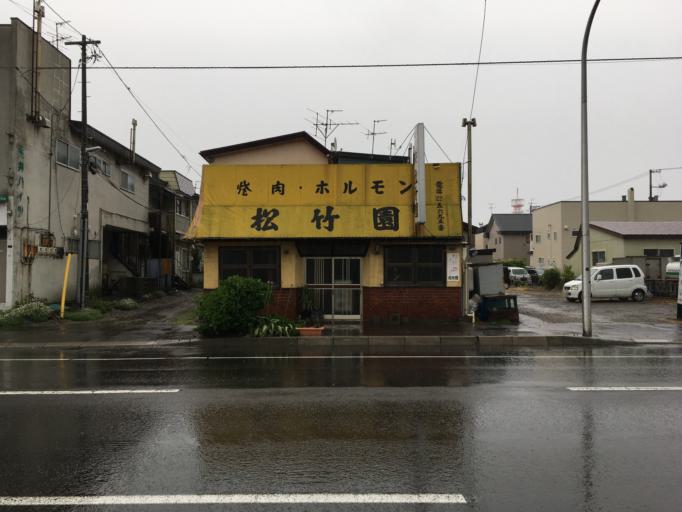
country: JP
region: Hokkaido
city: Hakodate
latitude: 41.7780
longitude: 140.7344
